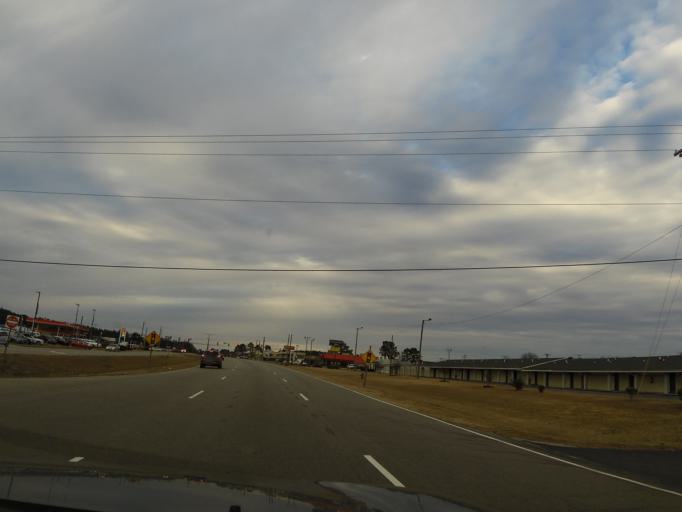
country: US
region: North Carolina
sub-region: Nash County
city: Rocky Mount
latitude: 35.9837
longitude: -77.7850
